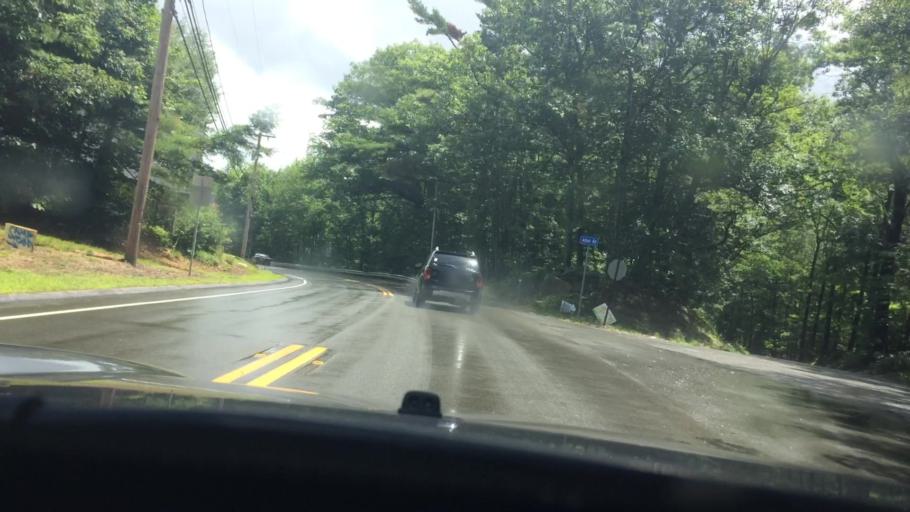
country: US
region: Massachusetts
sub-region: Worcester County
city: Phillipston
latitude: 42.5703
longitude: -72.1550
